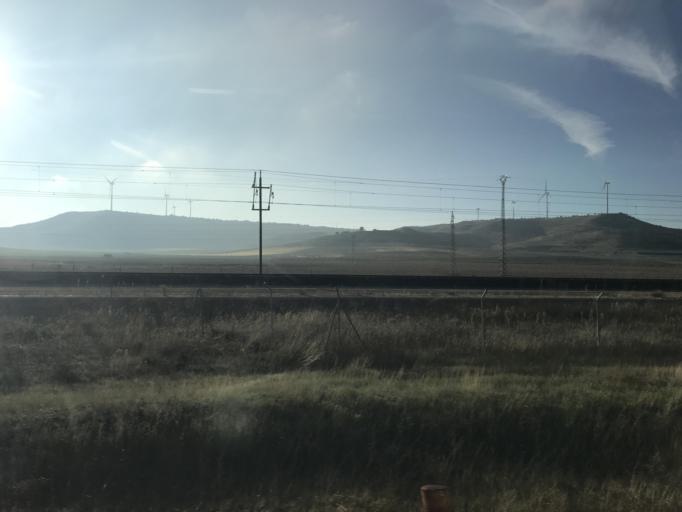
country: ES
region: Castille and Leon
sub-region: Provincia de Palencia
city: Torquemada
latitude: 42.0258
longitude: -4.2829
